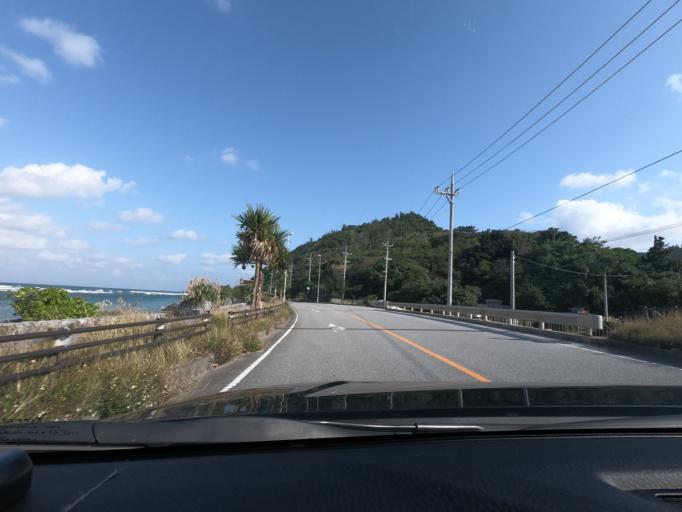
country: JP
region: Okinawa
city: Nago
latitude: 26.7569
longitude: 128.1888
